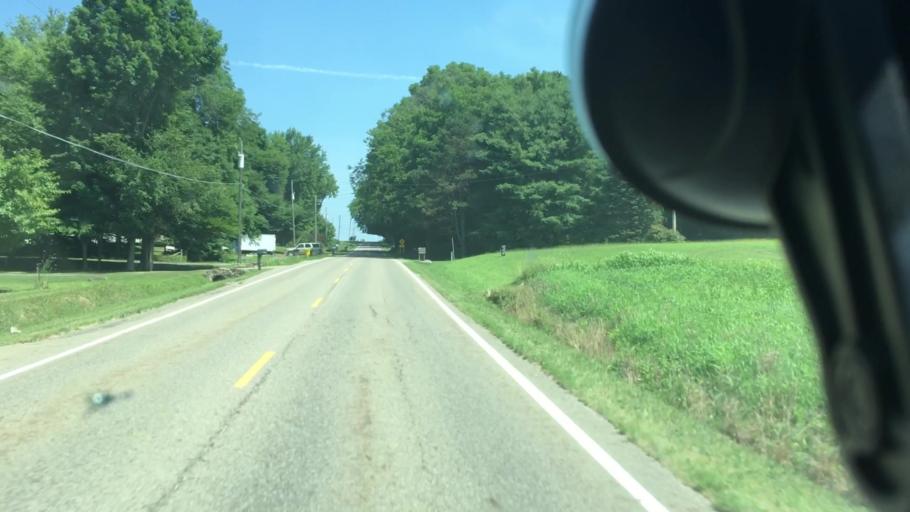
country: US
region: Ohio
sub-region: Columbiana County
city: Lisbon
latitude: 40.7992
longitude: -80.8586
